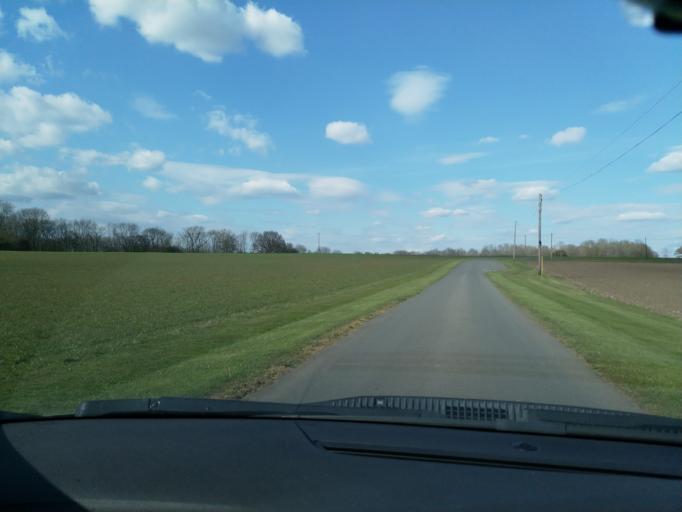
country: GB
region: England
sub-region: Warwickshire
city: Wellesbourne Mountford
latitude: 52.1739
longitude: -1.5706
